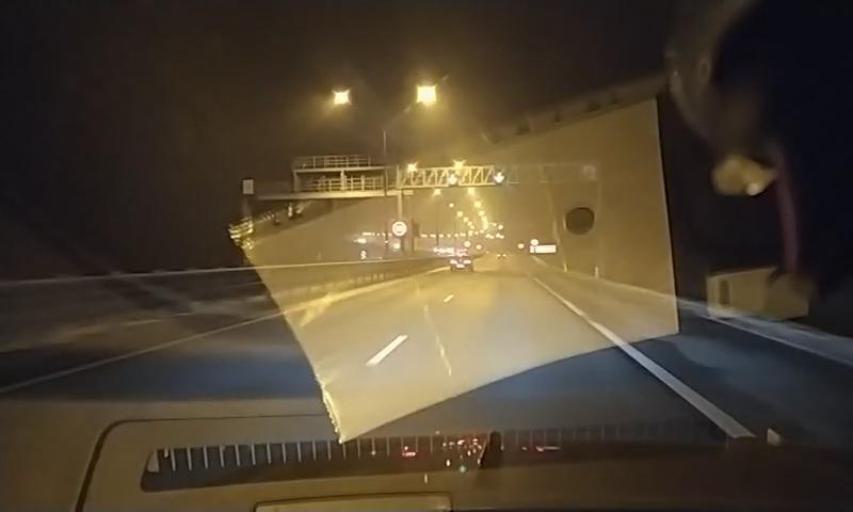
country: RU
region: Leningrad
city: Bugry
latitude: 60.1048
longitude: 30.3861
